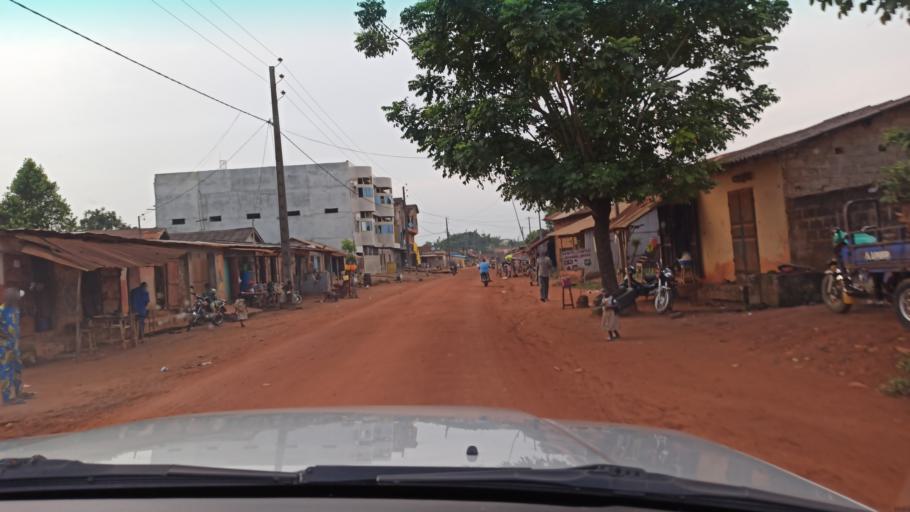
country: BJ
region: Queme
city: Porto-Novo
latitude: 6.5284
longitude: 2.6671
